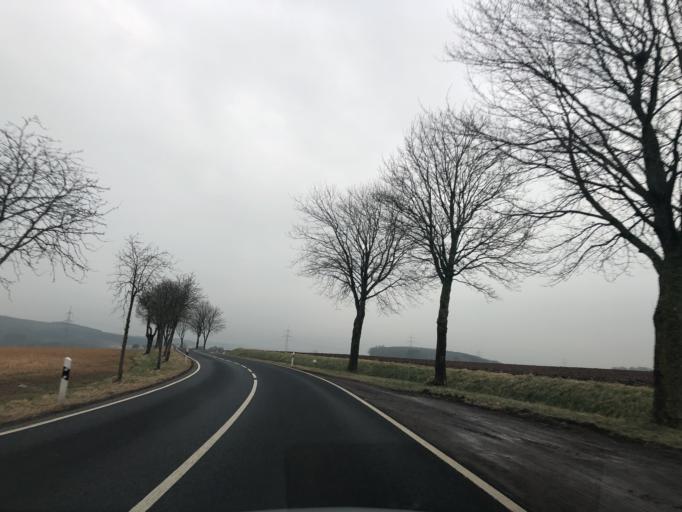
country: DE
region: Hesse
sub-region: Regierungsbezirk Darmstadt
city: Birstein
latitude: 50.3631
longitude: 9.3096
